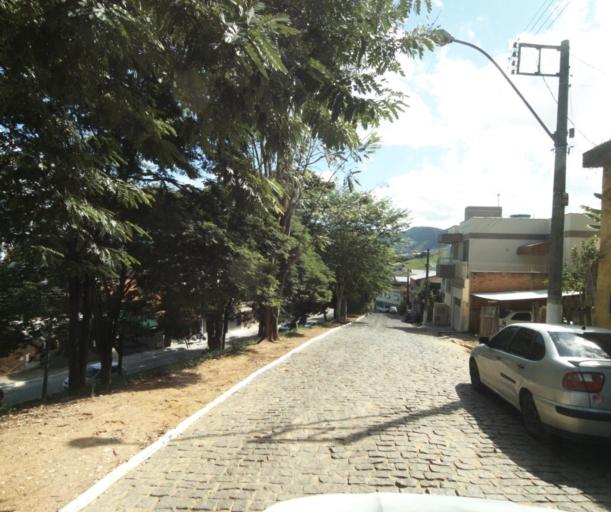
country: BR
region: Espirito Santo
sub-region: Sao Jose Do Calcado
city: Sao Jose do Calcado
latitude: -21.0234
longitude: -41.6535
